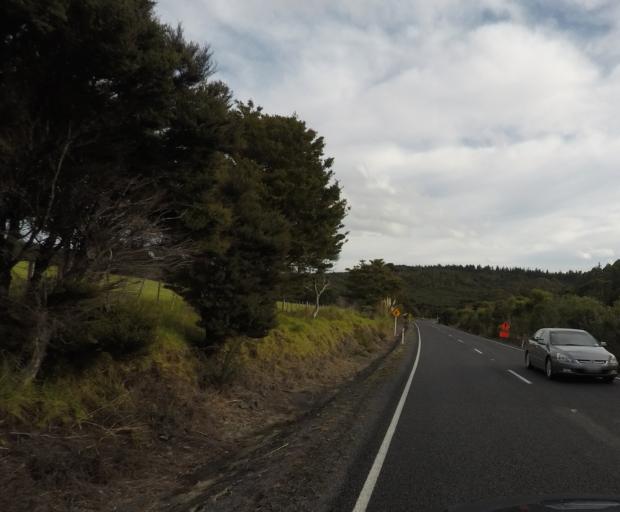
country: NZ
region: Northland
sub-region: Whangarei
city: Ruakaka
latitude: -36.0566
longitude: 174.5579
